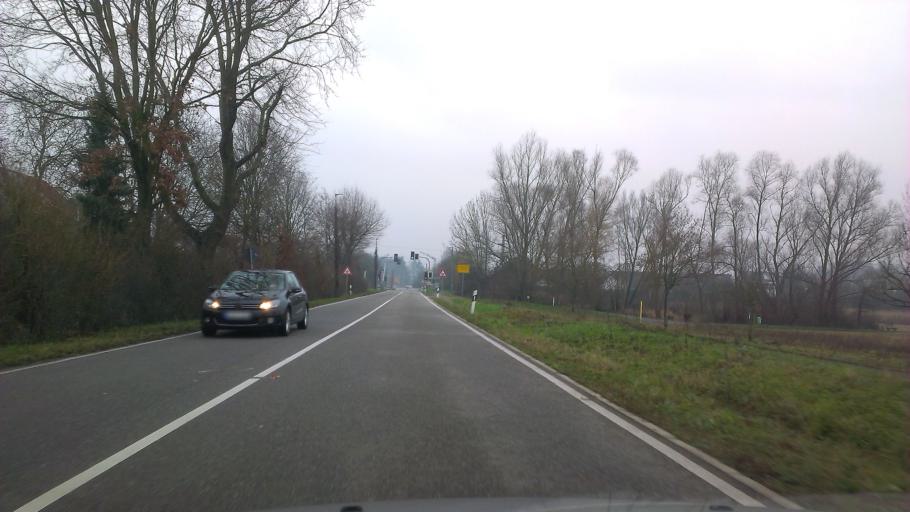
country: DE
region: Baden-Wuerttemberg
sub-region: Karlsruhe Region
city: Ubstadt-Weiher
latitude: 49.1600
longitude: 8.6259
